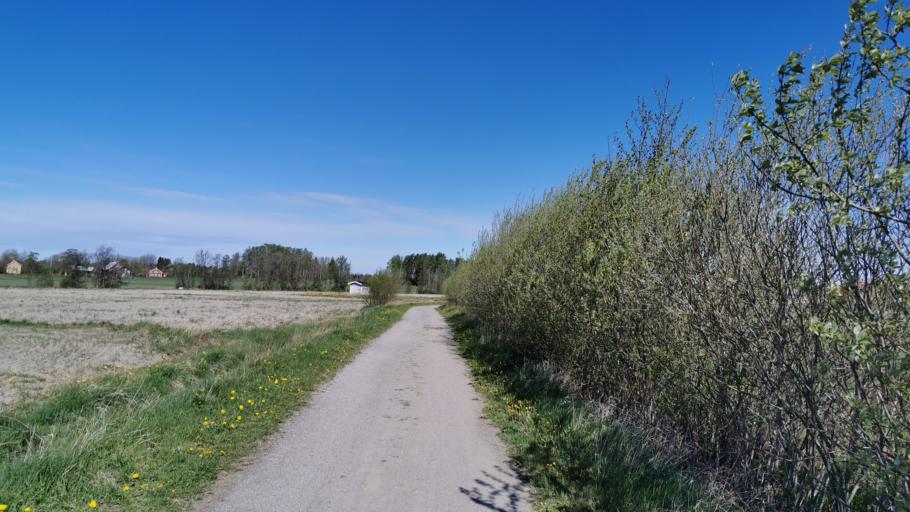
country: SE
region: OErebro
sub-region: Orebro Kommun
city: Orebro
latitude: 59.3114
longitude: 15.2149
